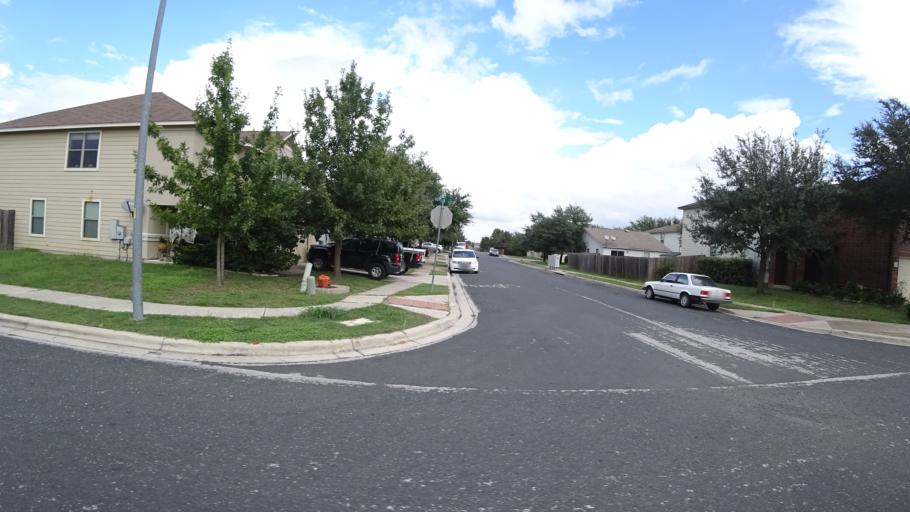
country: US
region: Texas
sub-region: Travis County
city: Onion Creek
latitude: 30.1533
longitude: -97.7431
